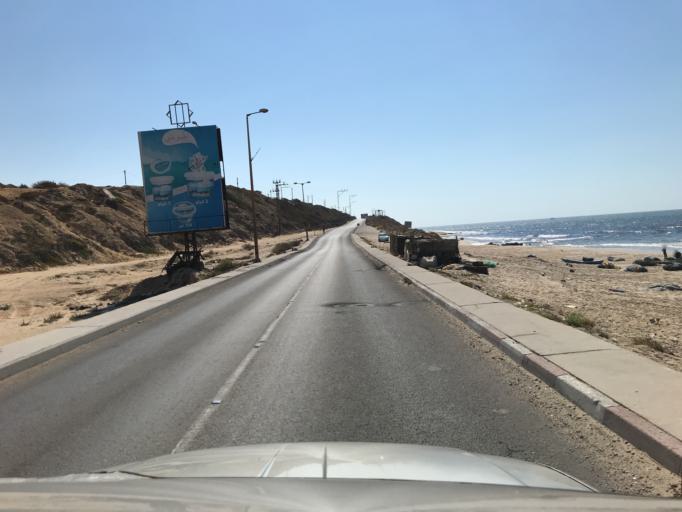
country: PS
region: Gaza Strip
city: An Nusayrat
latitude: 31.4625
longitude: 34.3748
